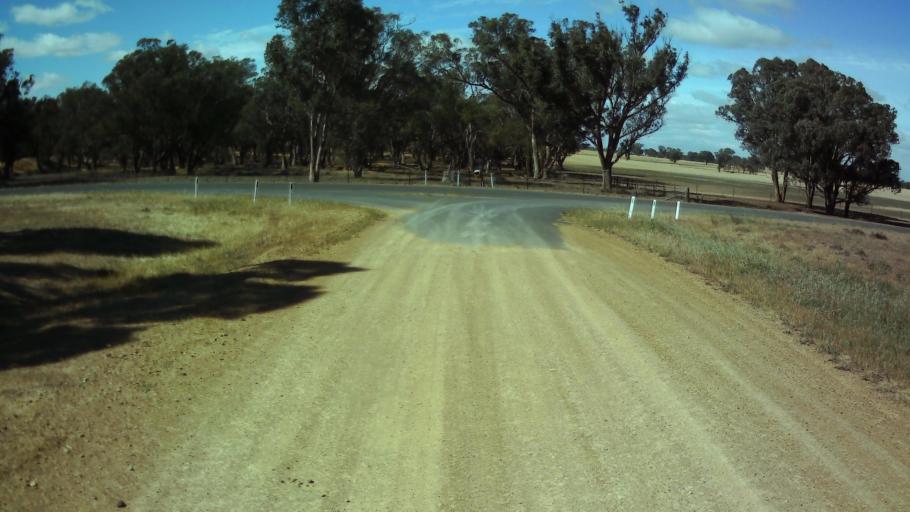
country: AU
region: New South Wales
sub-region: Weddin
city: Grenfell
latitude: -34.0651
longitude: 148.3113
